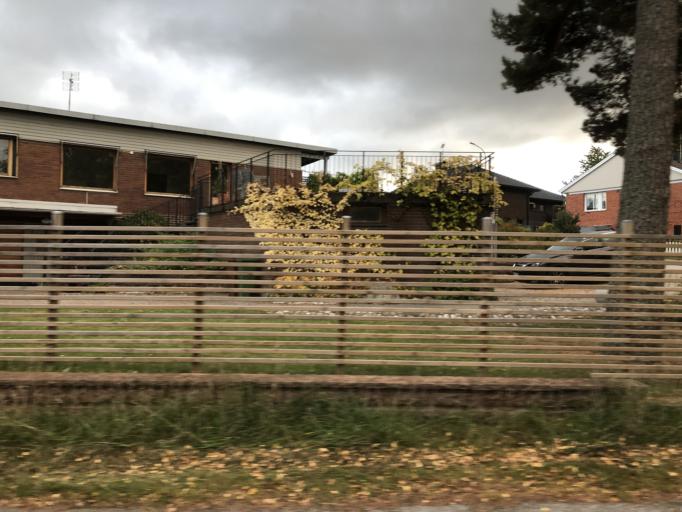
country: SE
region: Stockholm
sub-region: Jarfalla Kommun
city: Jakobsberg
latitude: 59.4292
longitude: 17.8145
